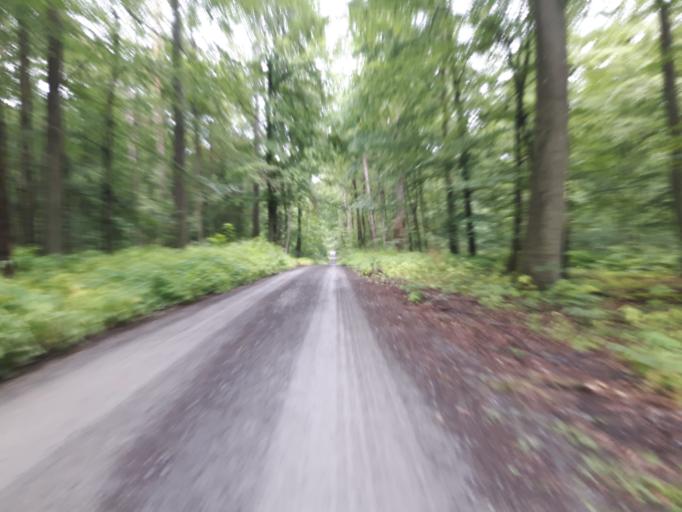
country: DE
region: Baden-Wuerttemberg
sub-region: Regierungsbezirk Stuttgart
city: Eppingen
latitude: 49.1158
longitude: 8.9391
